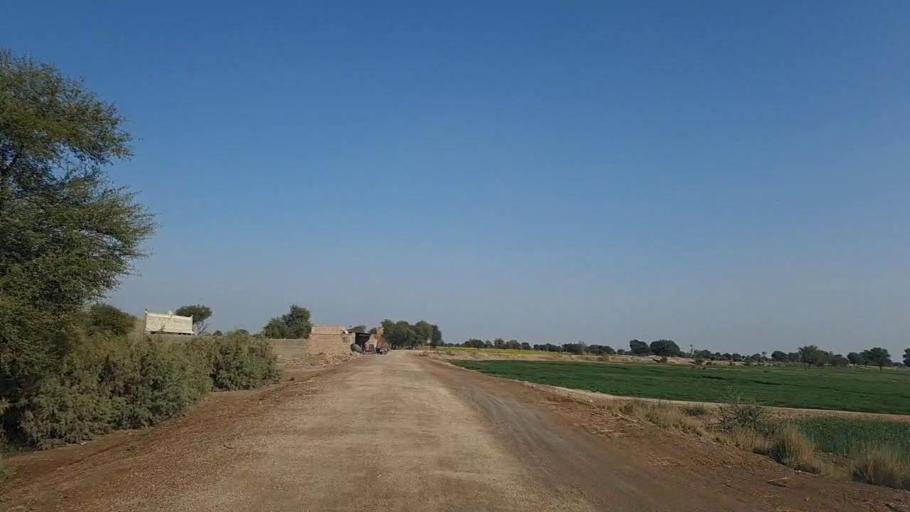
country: PK
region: Sindh
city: Shahpur Chakar
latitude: 26.2050
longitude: 68.6422
